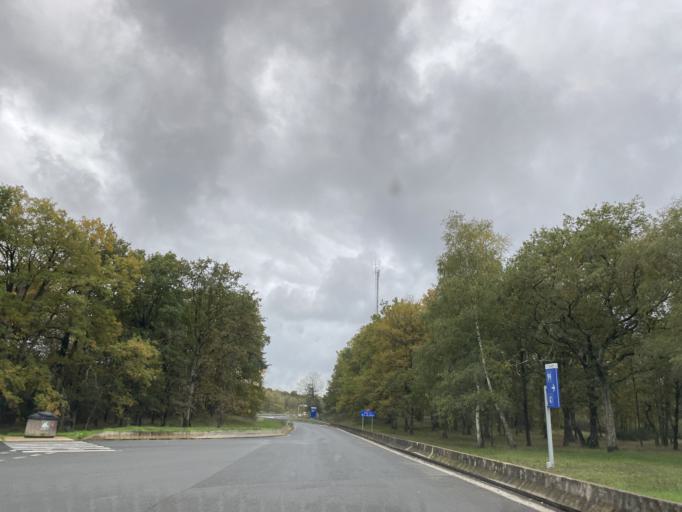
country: FR
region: Centre
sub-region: Departement du Loiret
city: Saint-Hilaire-Saint-Mesmin
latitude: 47.8097
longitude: 1.8524
